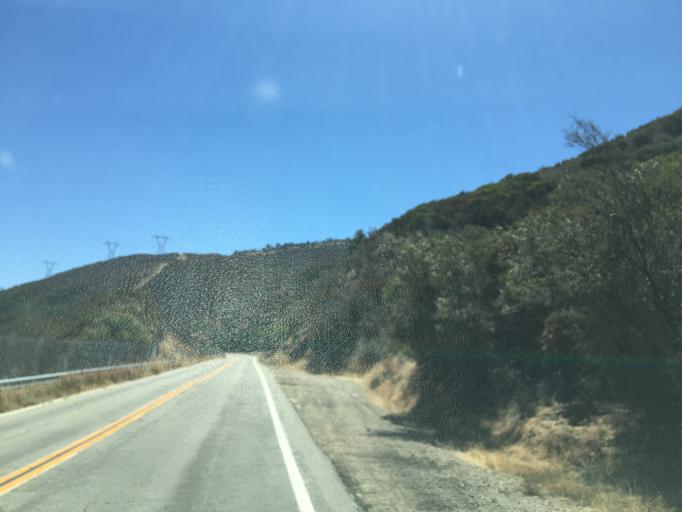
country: US
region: California
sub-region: Los Angeles County
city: Green Valley
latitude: 34.5765
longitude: -118.3788
